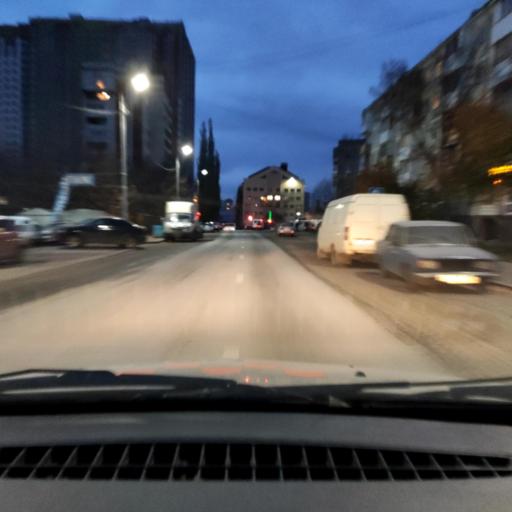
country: RU
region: Bashkortostan
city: Ufa
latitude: 54.7276
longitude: 55.9825
